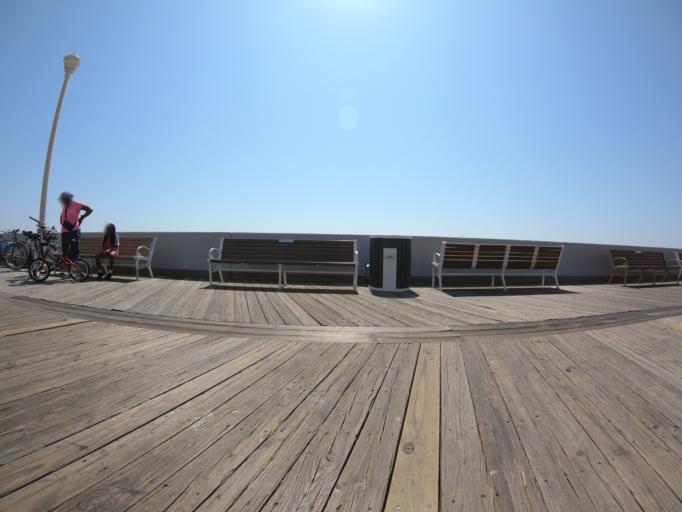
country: US
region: Maryland
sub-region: Worcester County
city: Ocean City
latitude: 38.3357
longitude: -75.0826
